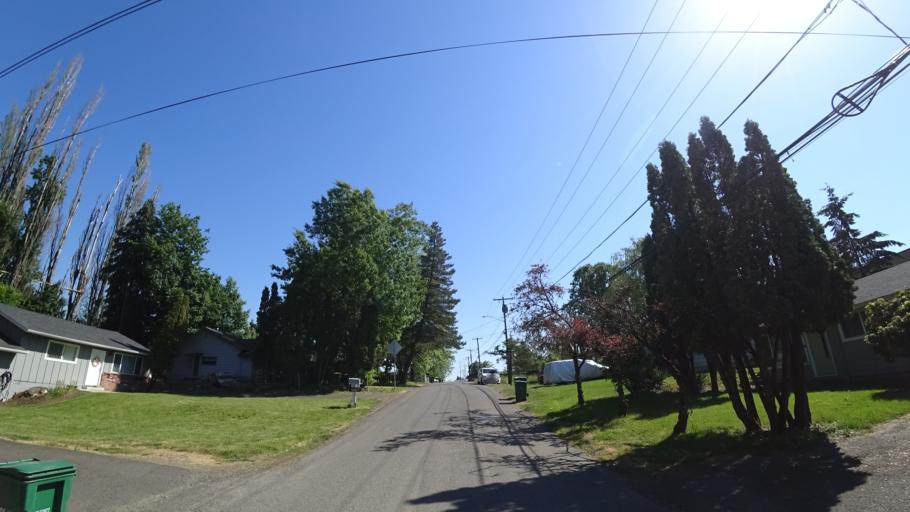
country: US
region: Oregon
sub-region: Washington County
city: Beaverton
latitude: 45.4920
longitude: -122.8247
